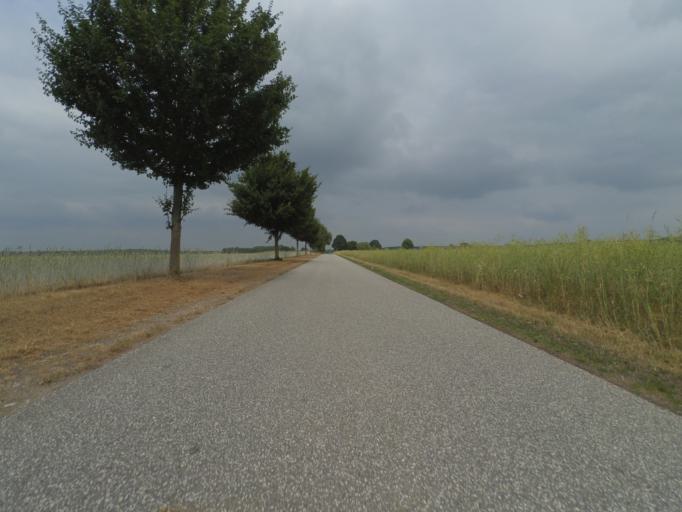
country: DE
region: Mecklenburg-Vorpommern
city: Plau am See
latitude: 53.4226
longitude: 12.1497
